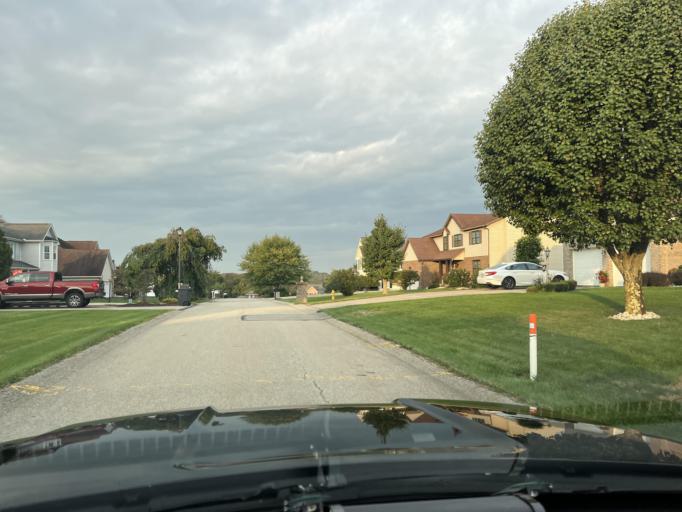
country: US
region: Pennsylvania
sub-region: Fayette County
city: South Uniontown
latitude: 39.8963
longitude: -79.7697
